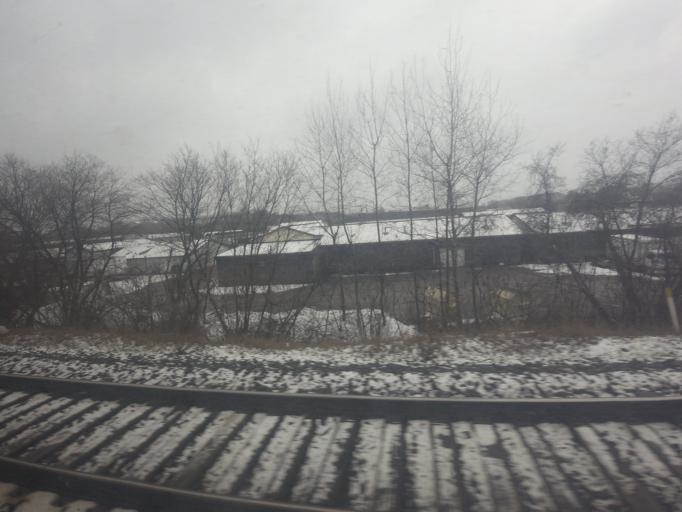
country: CA
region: Ontario
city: Quinte West
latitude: 44.1178
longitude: -77.5963
